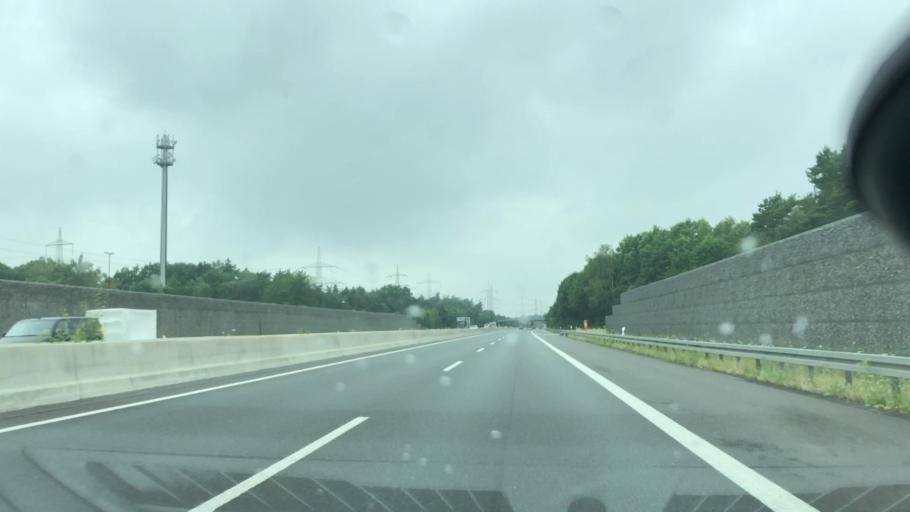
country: DE
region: North Rhine-Westphalia
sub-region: Regierungsbezirk Detmold
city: Hovelhof
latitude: 51.8391
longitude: 8.6840
